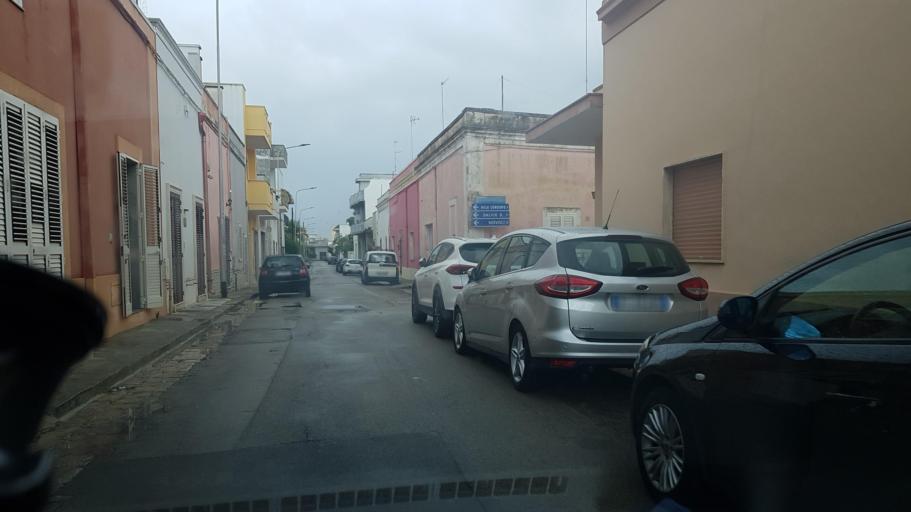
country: IT
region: Apulia
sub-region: Provincia di Lecce
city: Carmiano
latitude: 40.3482
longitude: 18.0449
